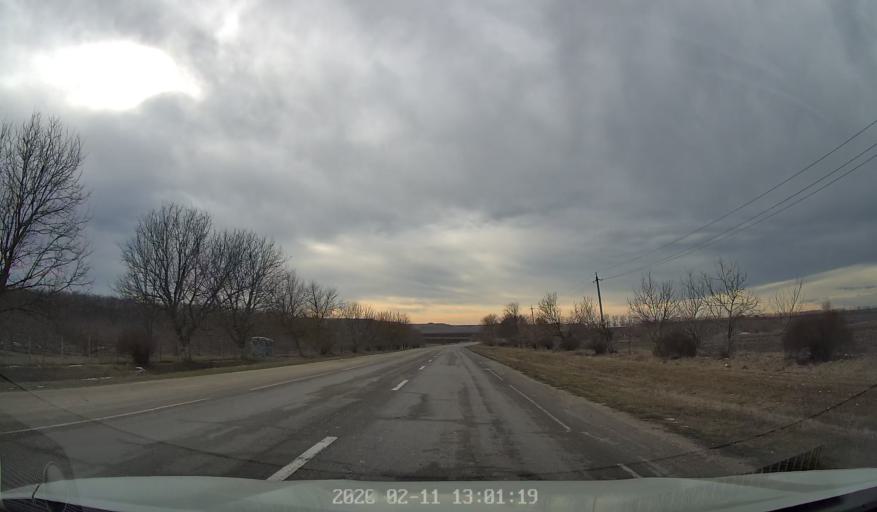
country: MD
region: Briceni
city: Briceni
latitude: 48.3193
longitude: 27.0039
